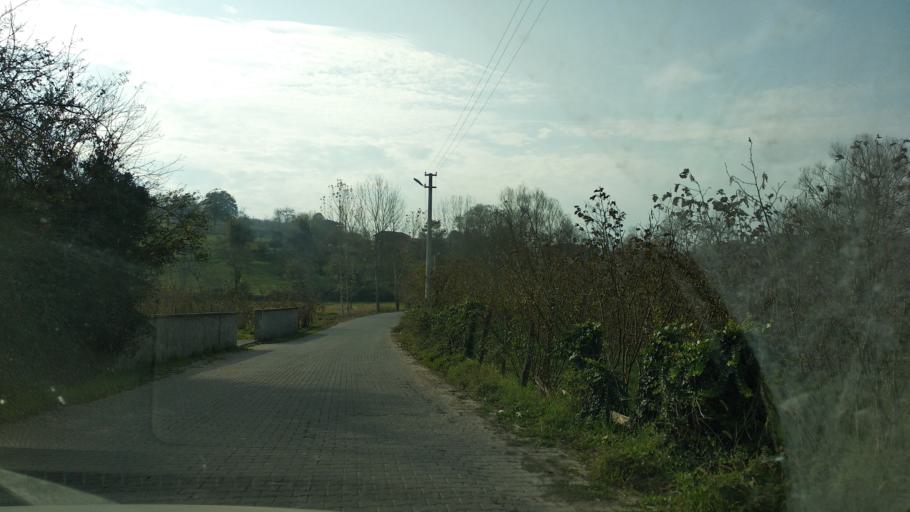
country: TR
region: Sakarya
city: Karasu
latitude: 41.0549
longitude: 30.6313
